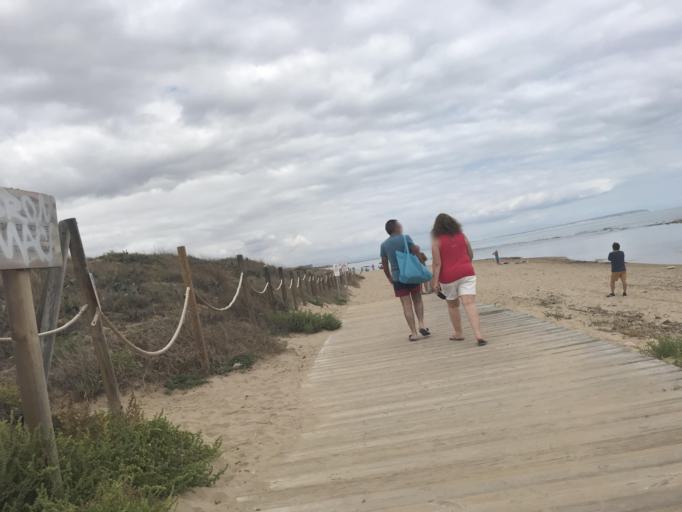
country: ES
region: Valencia
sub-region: Provincia de Alicante
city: Guardamar del Segura
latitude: 38.0306
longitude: -0.6512
